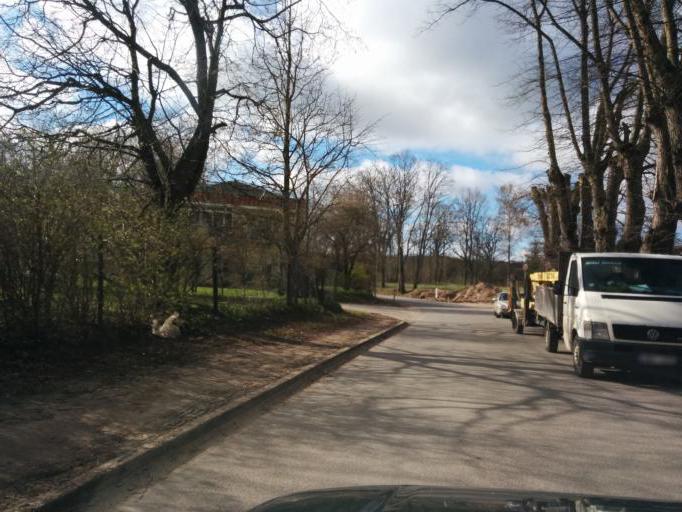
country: LV
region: Kekava
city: Balozi
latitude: 56.8916
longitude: 24.1550
